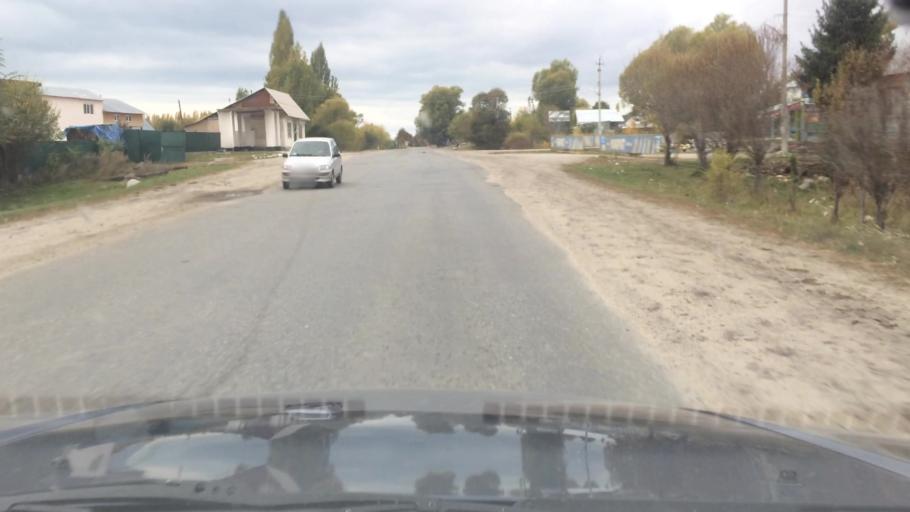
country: KG
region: Ysyk-Koel
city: Tyup
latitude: 42.7686
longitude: 78.1868
